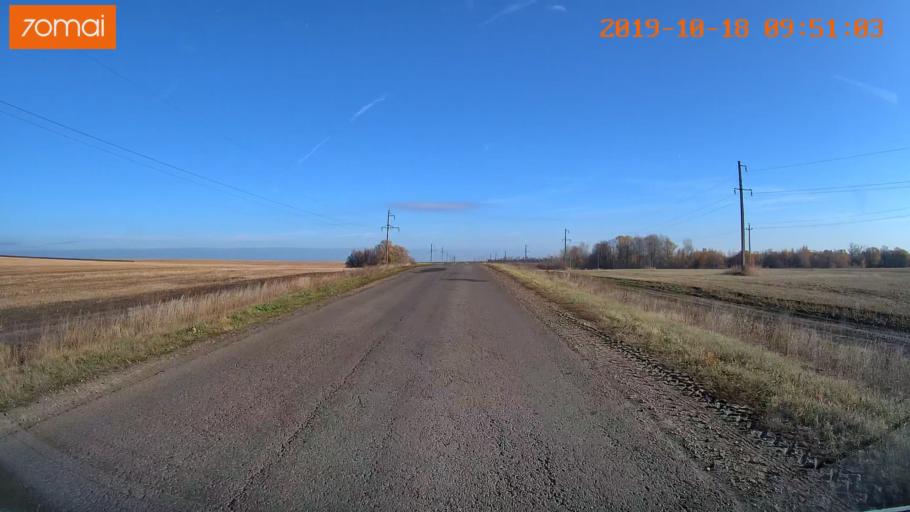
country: RU
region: Tula
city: Kazachka
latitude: 53.3359
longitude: 38.2864
